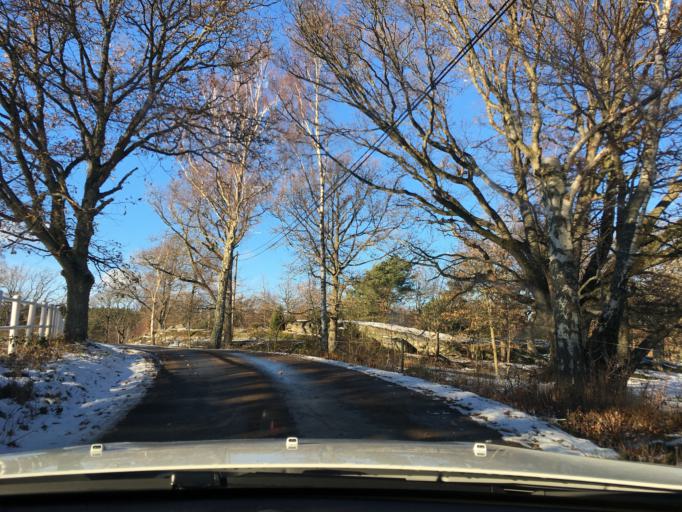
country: SE
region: Vaestra Goetaland
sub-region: Tjorns Kommun
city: Myggenas
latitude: 58.0965
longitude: 11.7690
